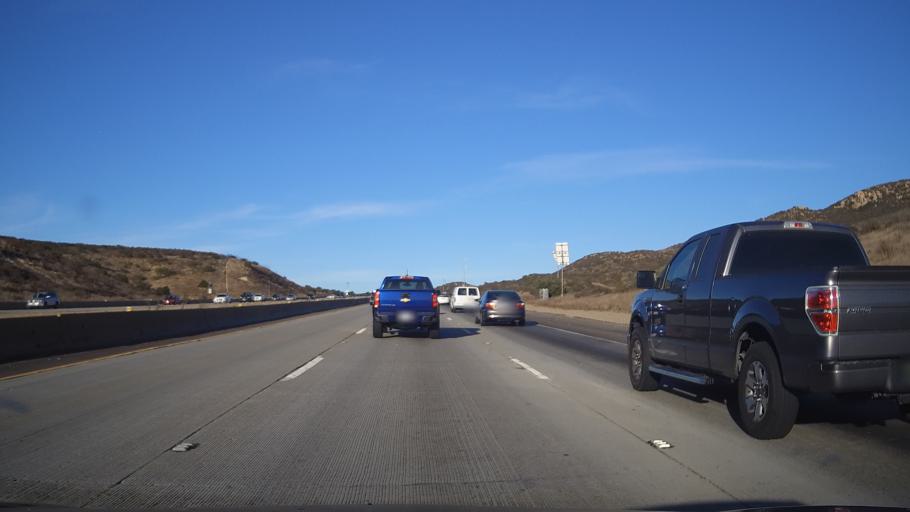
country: US
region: California
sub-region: San Diego County
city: La Mesa
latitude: 32.8490
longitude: -117.0751
